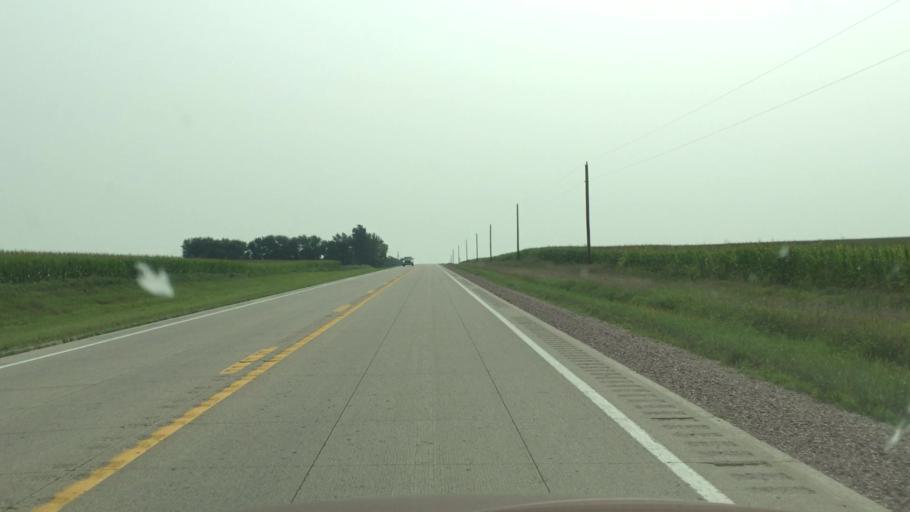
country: US
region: Iowa
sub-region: Osceola County
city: Sibley
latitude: 43.4327
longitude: -95.7008
